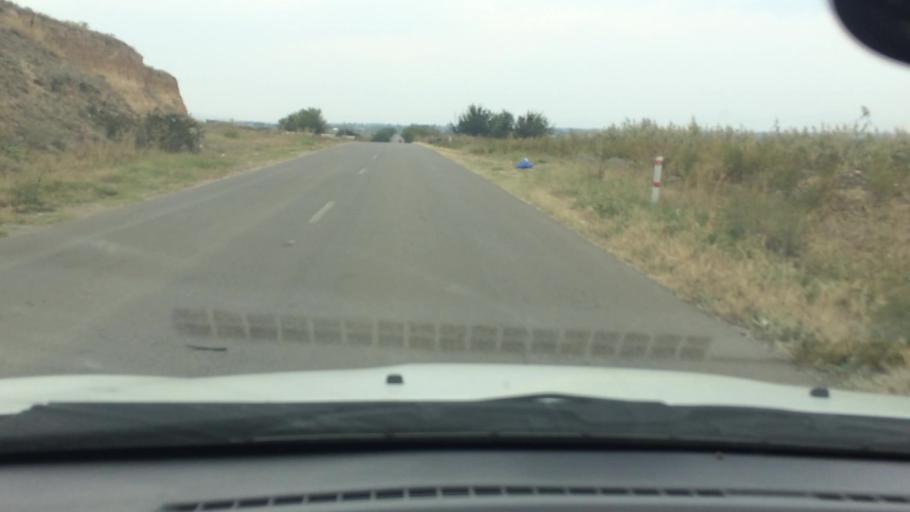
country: AM
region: Tavush
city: Berdavan
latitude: 41.3407
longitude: 44.9948
